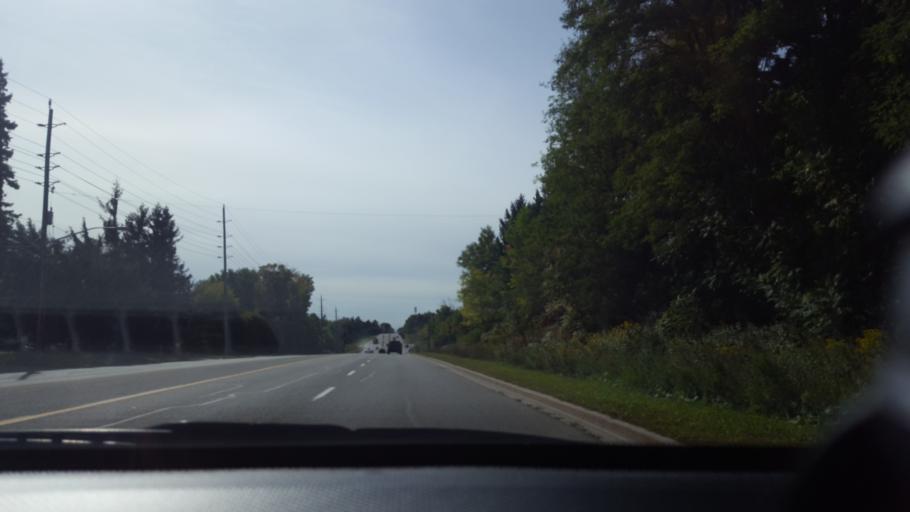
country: CA
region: Ontario
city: Newmarket
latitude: 43.9977
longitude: -79.4953
